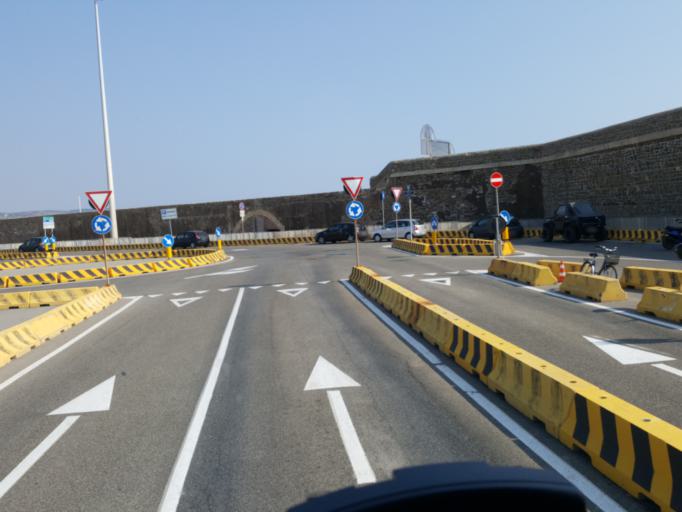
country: IT
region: Latium
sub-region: Citta metropolitana di Roma Capitale
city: Civitavecchia
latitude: 42.0894
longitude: 11.7868
